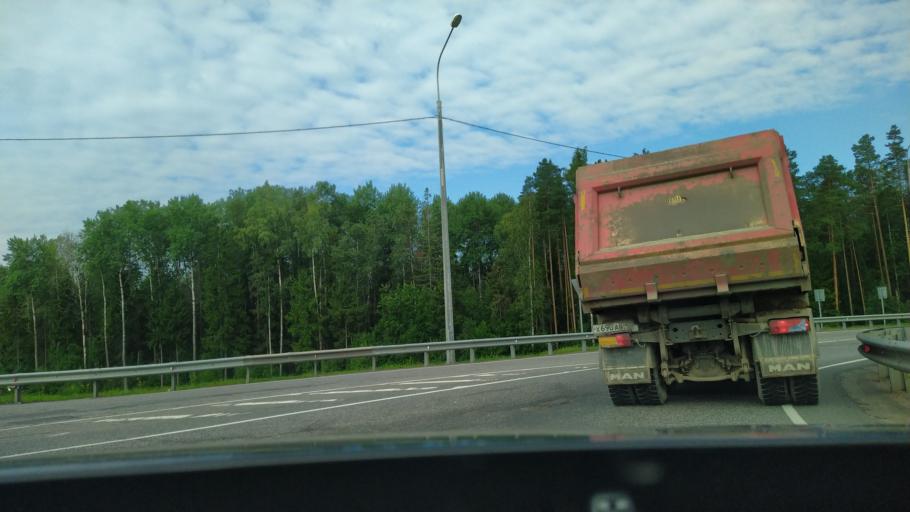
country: RU
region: Leningrad
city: Ul'yanovka
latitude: 59.6044
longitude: 30.7560
